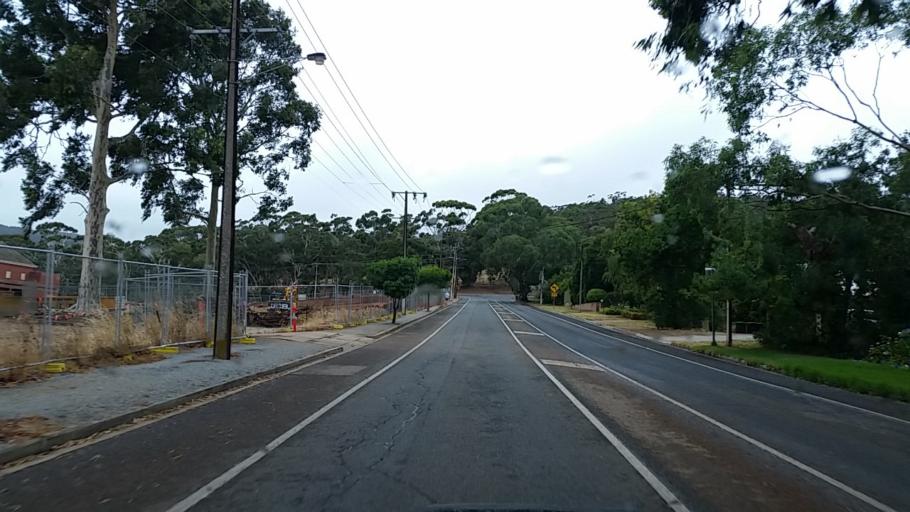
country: AU
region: South Australia
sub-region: Adelaide Hills
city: Adelaide Hills
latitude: -34.9002
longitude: 138.6889
